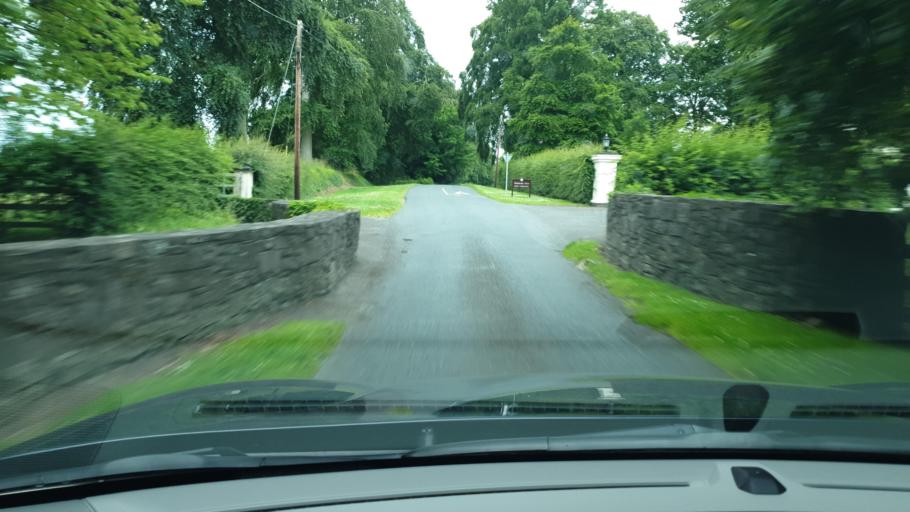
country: IE
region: Leinster
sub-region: An Mhi
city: Dunboyne
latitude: 53.4430
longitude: -6.4768
